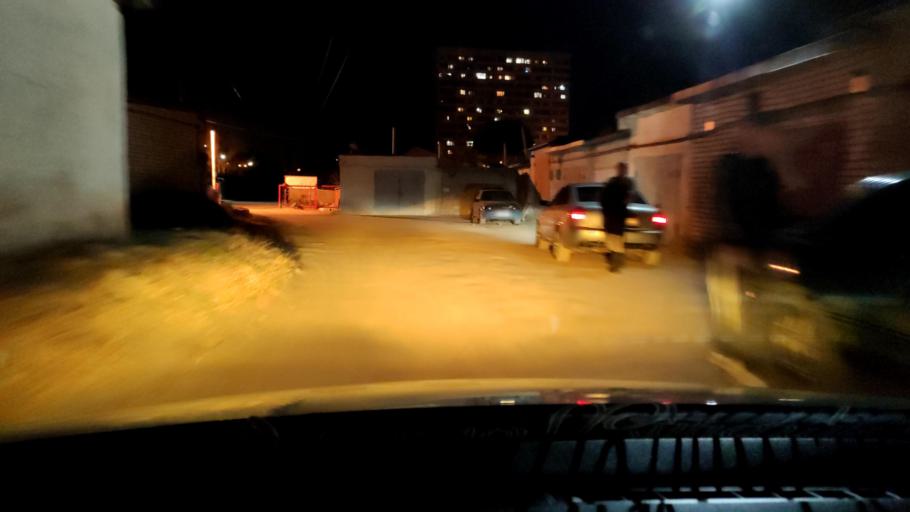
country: RU
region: Voronezj
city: Pridonskoy
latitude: 51.6888
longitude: 39.0775
